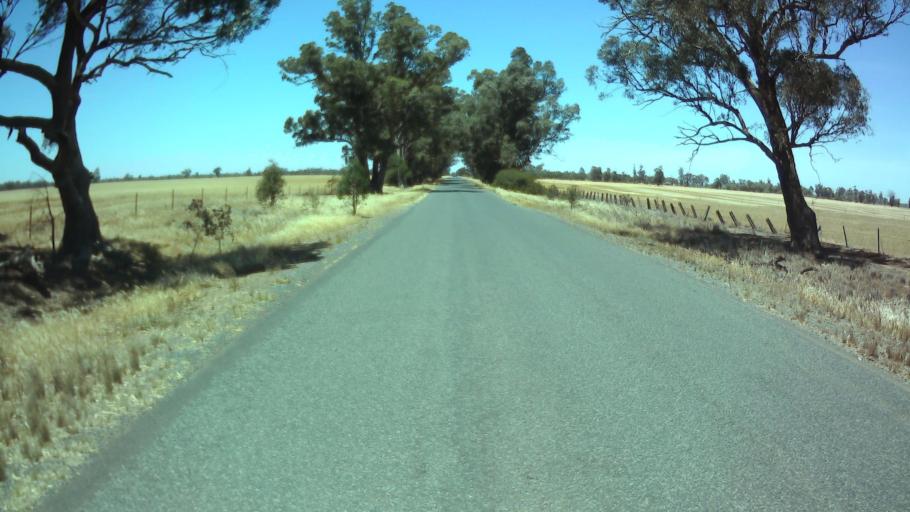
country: AU
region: New South Wales
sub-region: Weddin
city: Grenfell
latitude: -34.0217
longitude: 147.7925
